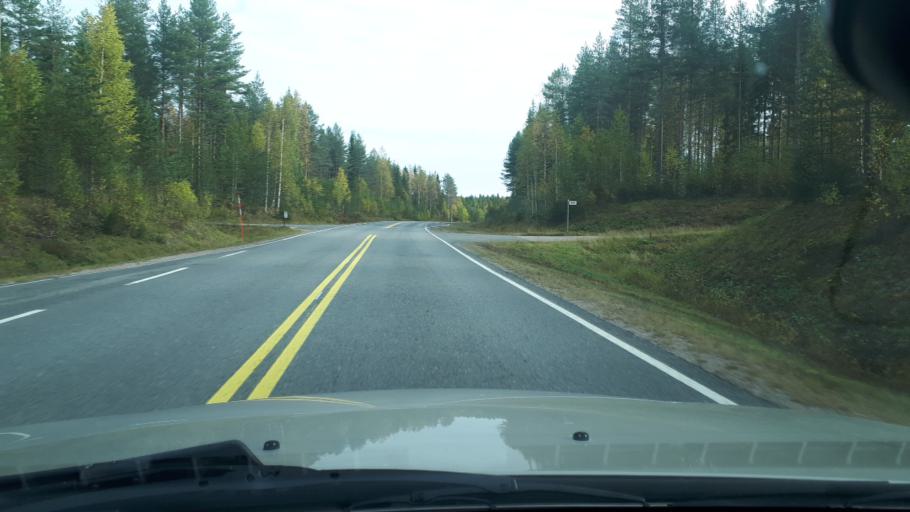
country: FI
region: Lapland
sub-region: Rovaniemi
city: Ranua
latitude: 65.9670
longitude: 26.0005
